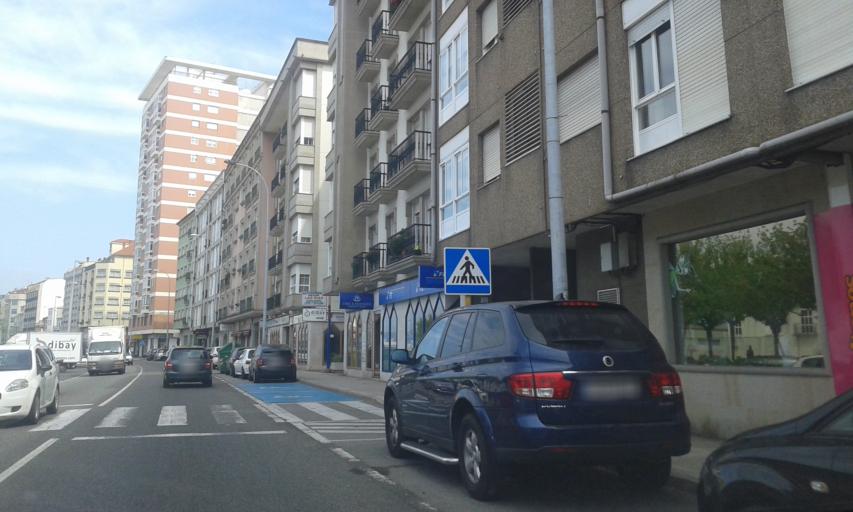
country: ES
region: Galicia
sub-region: Provincia de Pontevedra
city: Marin
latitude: 42.3941
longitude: -8.6945
